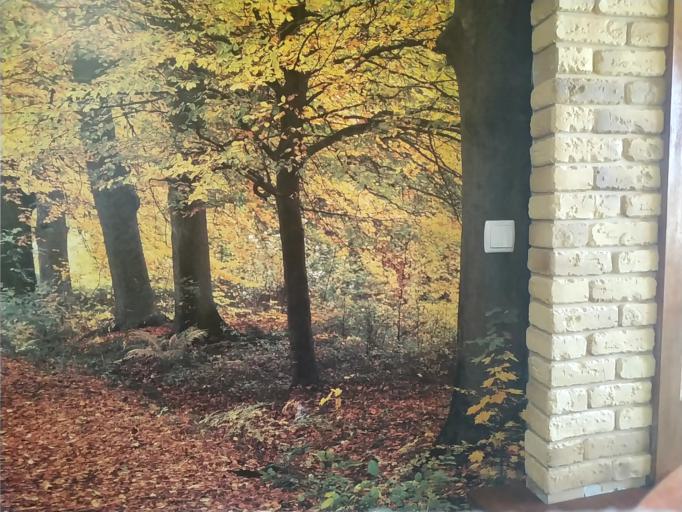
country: RU
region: Tverskaya
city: Krasnomayskiy
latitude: 57.7202
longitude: 34.4731
